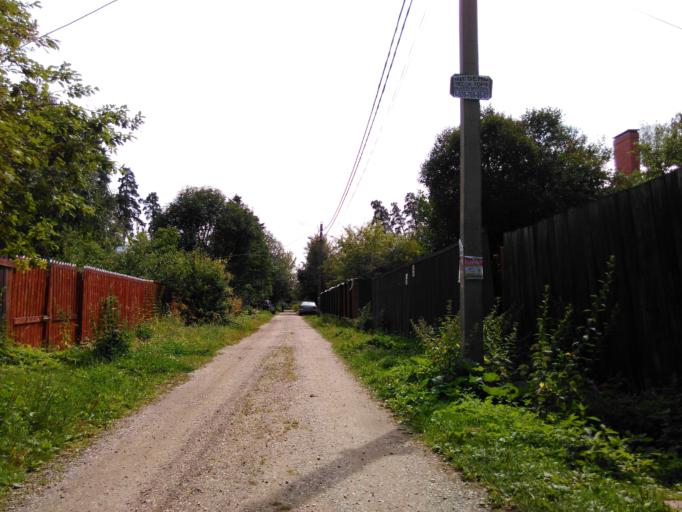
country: RU
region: Moskovskaya
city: Pravdinskiy
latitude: 56.0570
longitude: 37.8392
